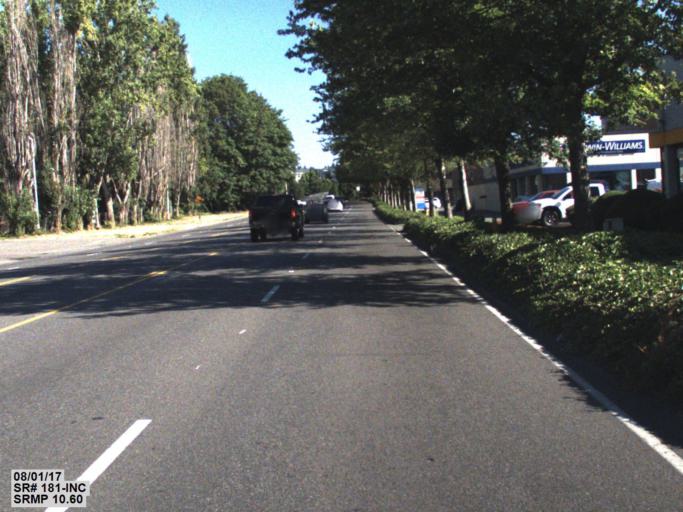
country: US
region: Washington
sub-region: King County
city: Tukwila
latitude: 47.4529
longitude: -122.2432
